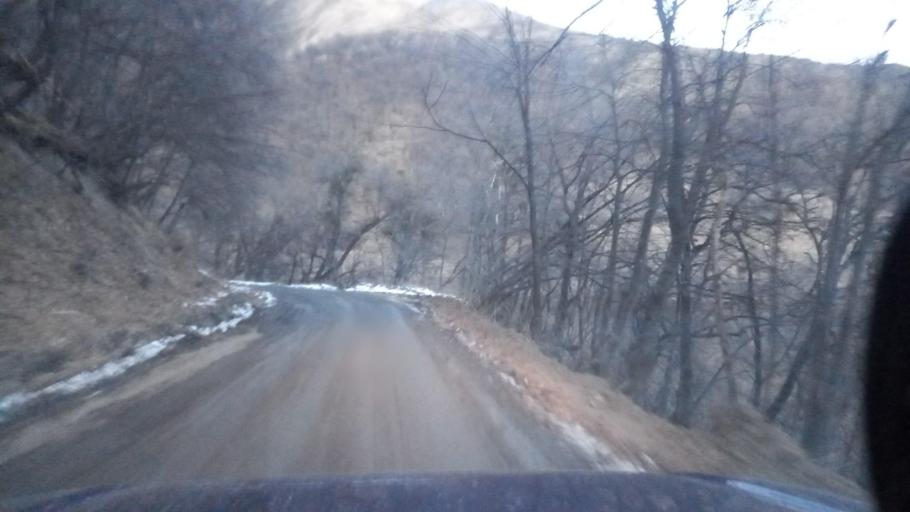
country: RU
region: Ingushetiya
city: Dzhayrakh
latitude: 42.8298
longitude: 44.5858
